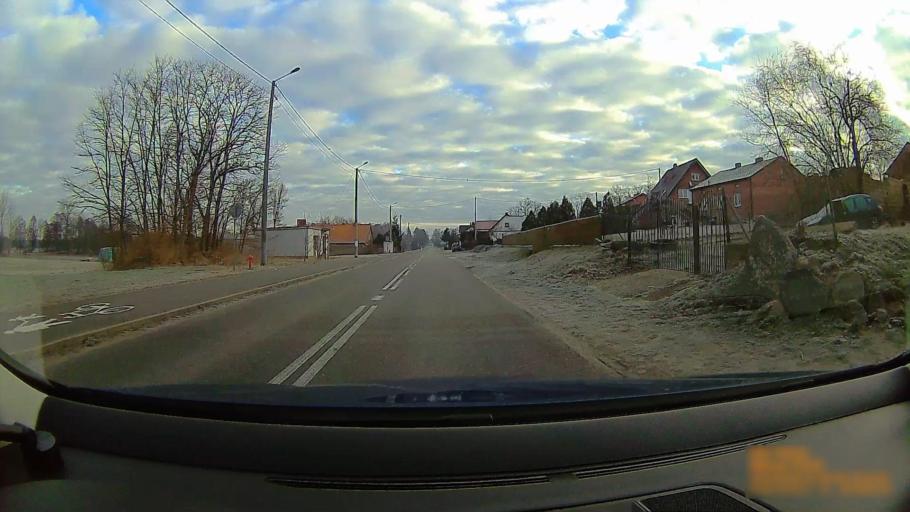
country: PL
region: Greater Poland Voivodeship
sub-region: Powiat koninski
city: Rzgow Pierwszy
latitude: 52.1697
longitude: 18.0858
